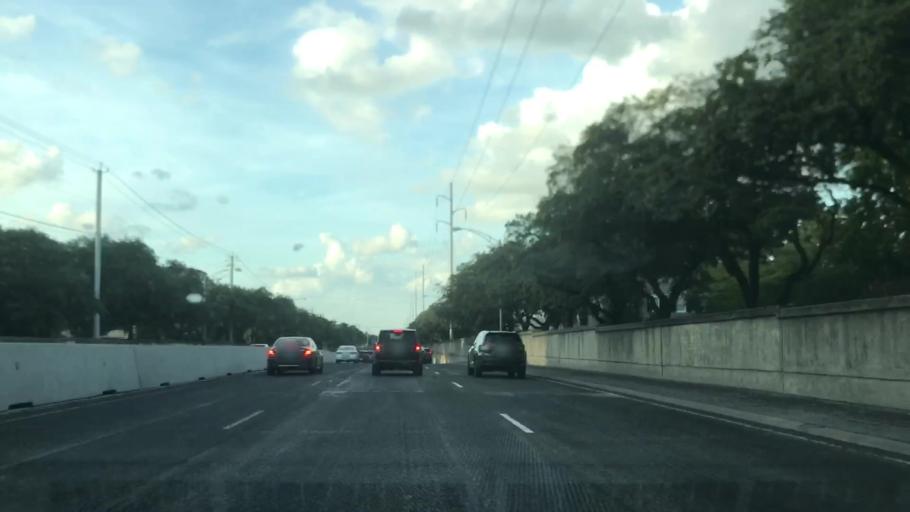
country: US
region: Texas
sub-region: Dallas County
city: Highland Park
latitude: 32.8299
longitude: -96.8157
